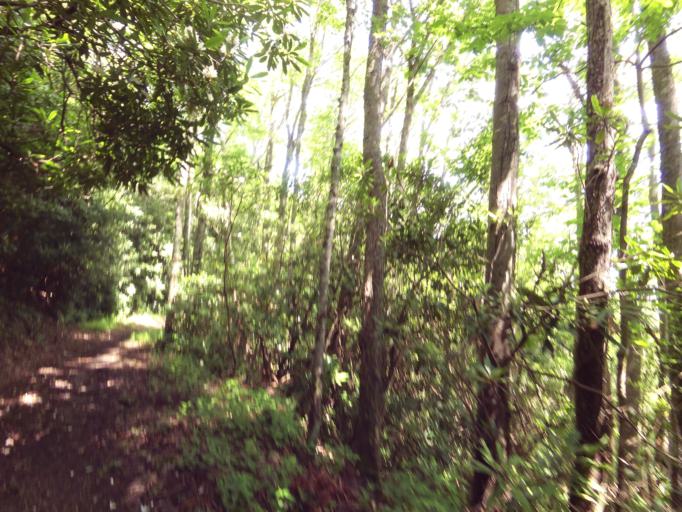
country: US
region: Tennessee
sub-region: Sevier County
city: Gatlinburg
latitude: 35.5852
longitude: -83.7346
